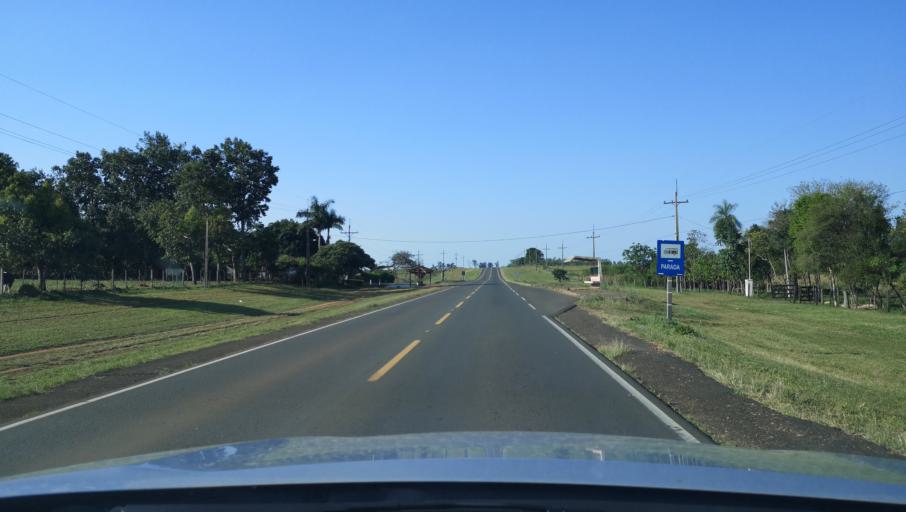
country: PY
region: Misiones
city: Santa Maria
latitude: -26.8163
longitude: -57.0243
